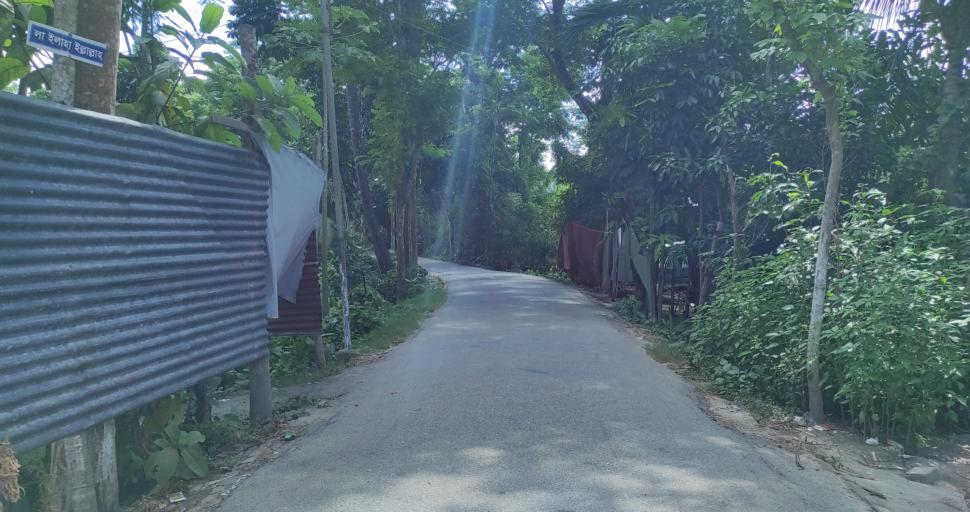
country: BD
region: Barisal
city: Gaurnadi
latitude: 22.9898
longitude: 90.2220
